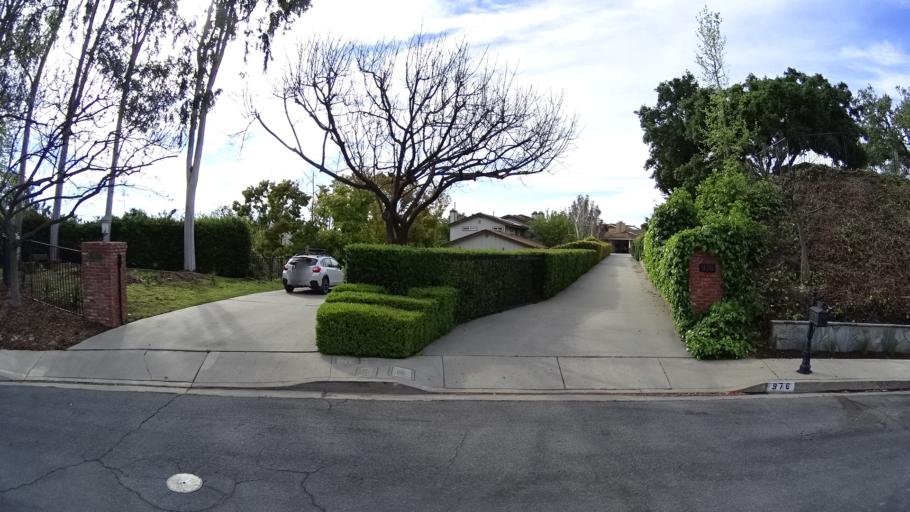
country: US
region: California
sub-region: Ventura County
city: Thousand Oaks
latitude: 34.1532
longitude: -118.8370
